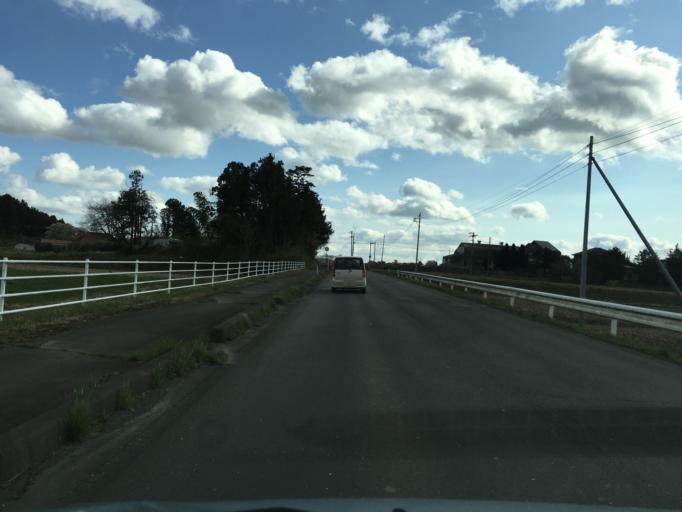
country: JP
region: Miyagi
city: Wakuya
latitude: 38.6546
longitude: 141.1923
